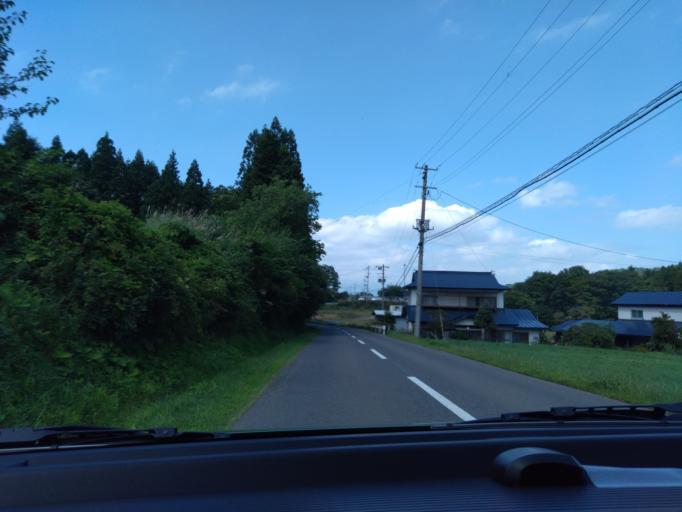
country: JP
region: Iwate
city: Shizukuishi
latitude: 39.6459
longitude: 140.9933
